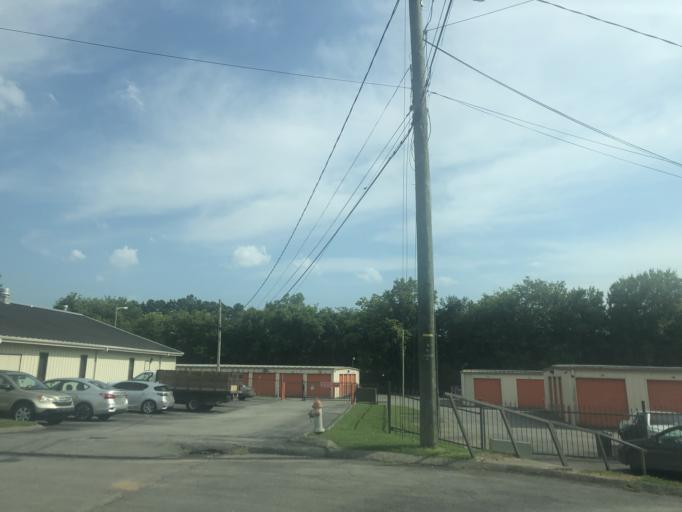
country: US
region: Tennessee
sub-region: Wilson County
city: Green Hill
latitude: 36.1716
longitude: -86.5982
